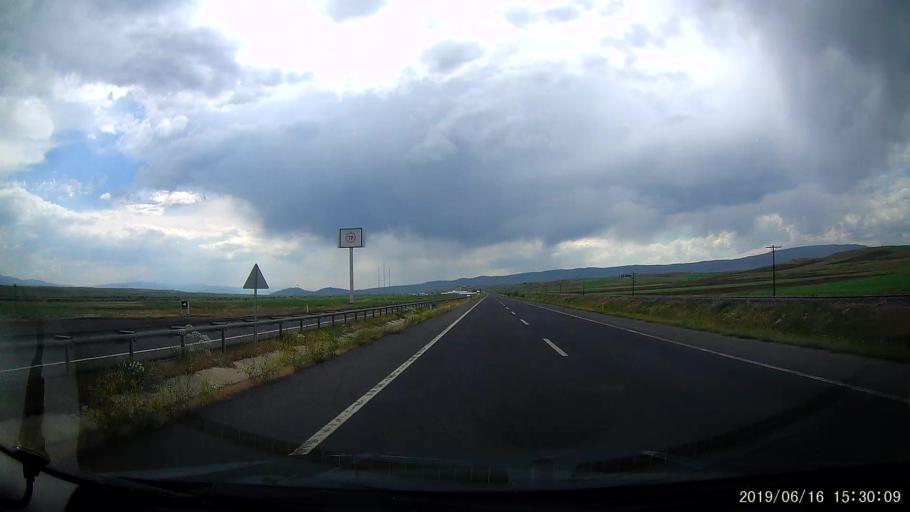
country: TR
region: Erzurum
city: Horasan
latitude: 40.0331
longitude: 42.1135
